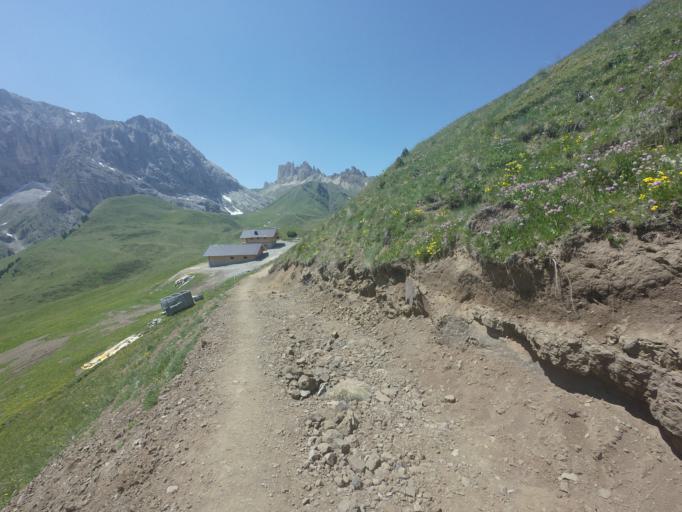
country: IT
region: Trentino-Alto Adige
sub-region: Provincia di Trento
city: Mazzin
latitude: 46.4966
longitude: 11.6626
